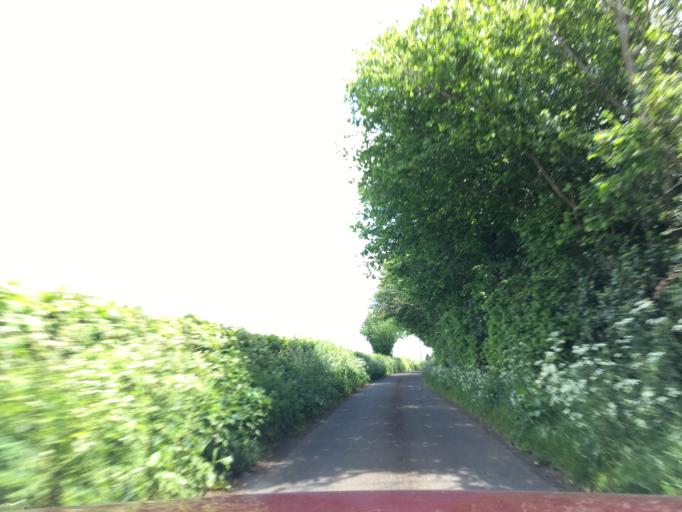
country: GB
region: England
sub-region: Gloucestershire
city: Painswick
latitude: 51.7864
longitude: -2.1439
